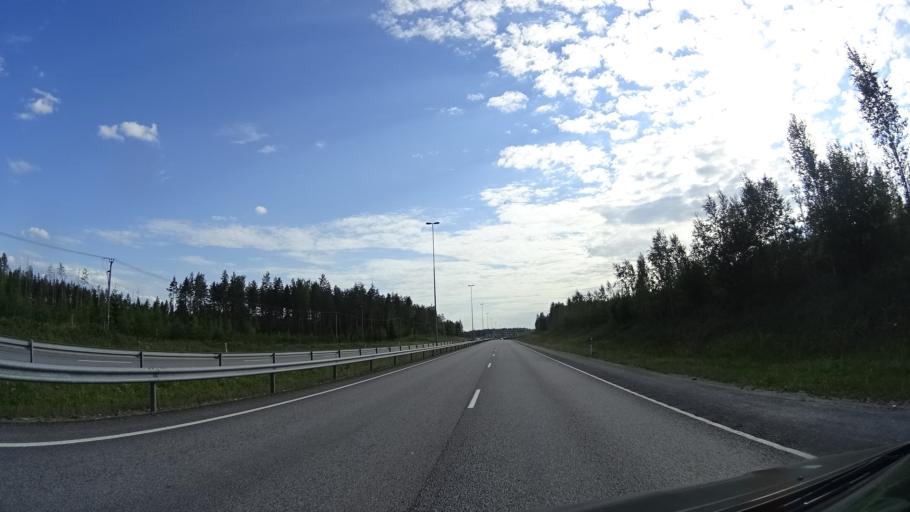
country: FI
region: South Karelia
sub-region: Lappeenranta
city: Joutseno
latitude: 61.0896
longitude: 28.3595
